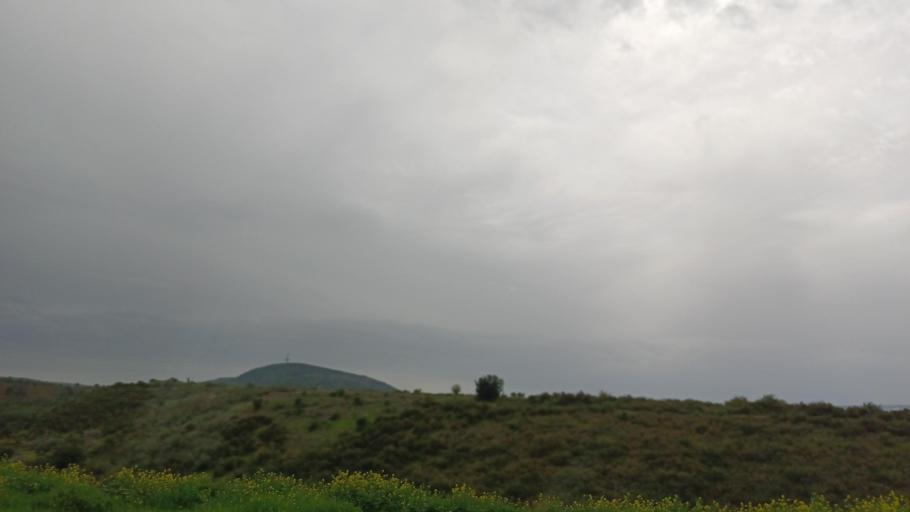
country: CY
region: Pafos
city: Polis
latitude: 35.0500
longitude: 32.4735
